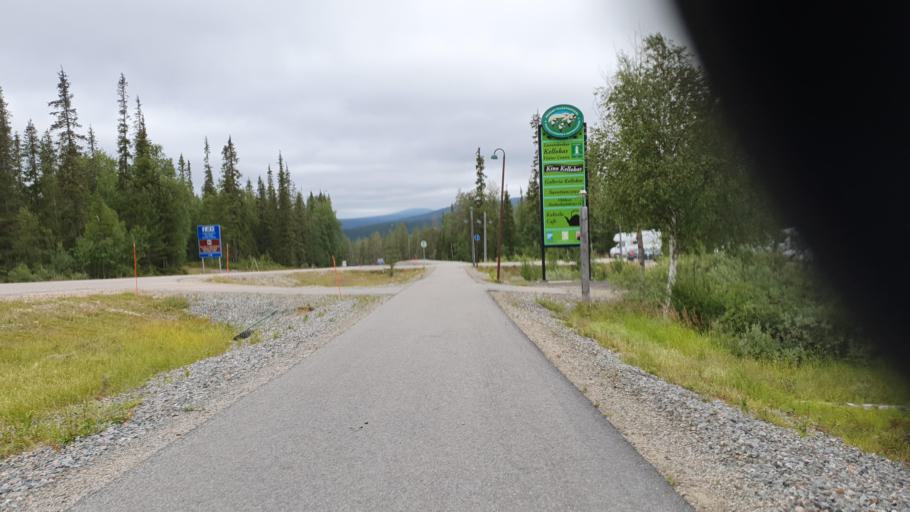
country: FI
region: Lapland
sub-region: Tunturi-Lappi
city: Kolari
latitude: 67.5892
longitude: 24.2017
